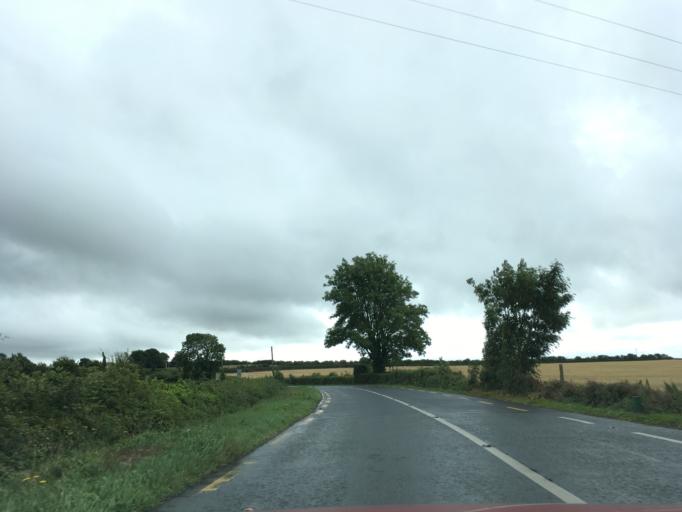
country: IE
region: Munster
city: Fethard
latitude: 52.4226
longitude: -7.7712
